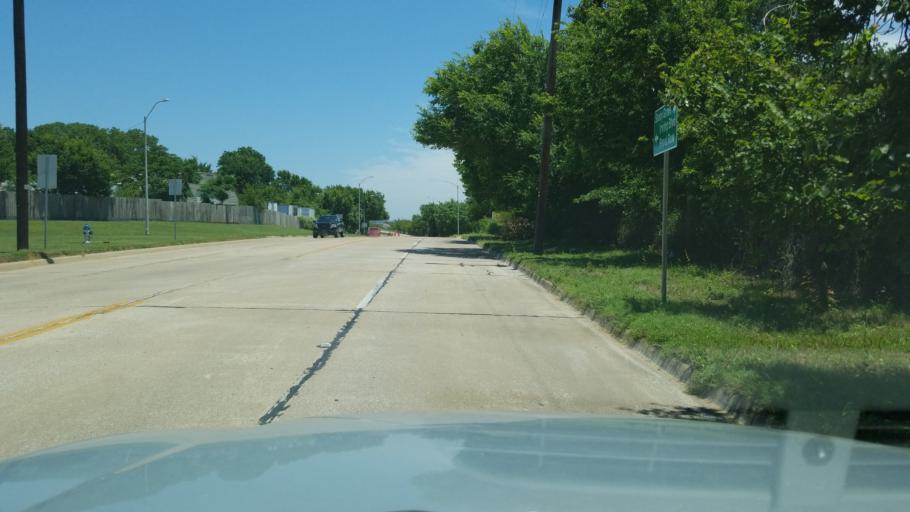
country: US
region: Texas
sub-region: Dallas County
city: Irving
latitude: 32.8020
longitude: -96.9077
